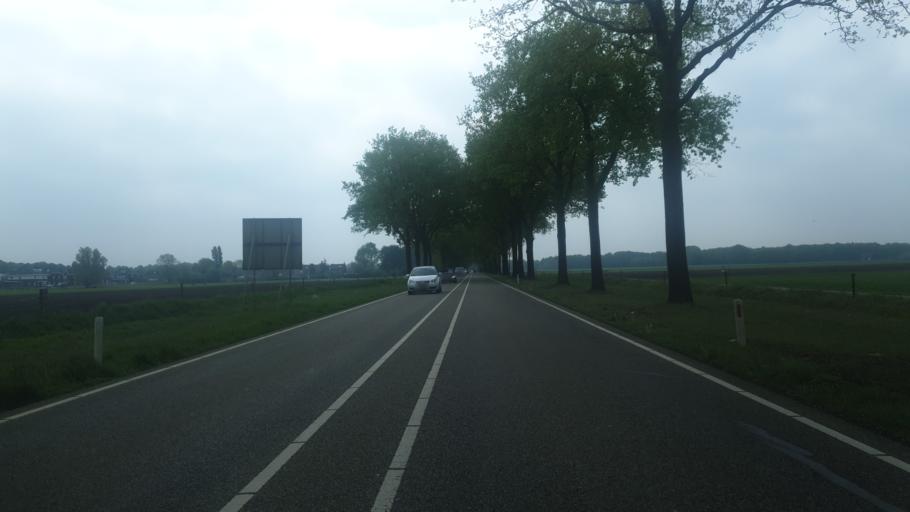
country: NL
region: North Brabant
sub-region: Gemeente Landerd
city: Zeeland
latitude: 51.7041
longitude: 5.6677
